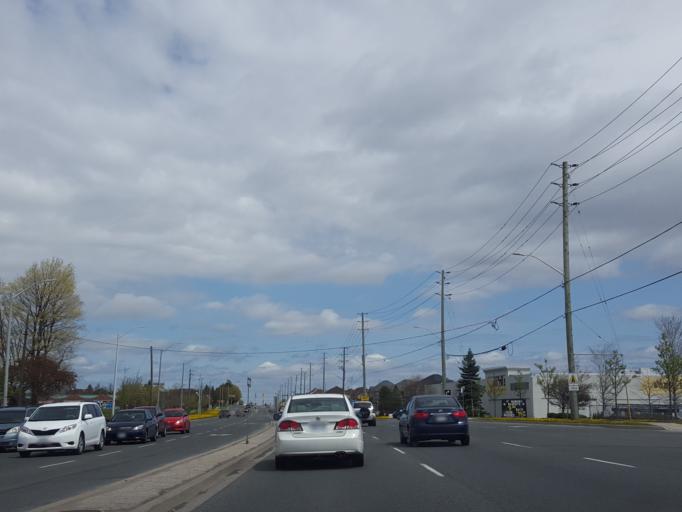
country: CA
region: Ontario
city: Markham
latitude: 43.8372
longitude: -79.2512
